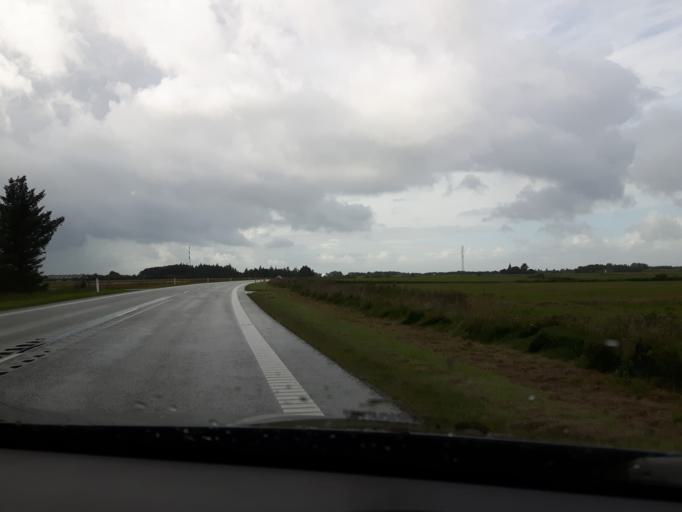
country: DK
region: North Denmark
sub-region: Jammerbugt Kommune
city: Fjerritslev
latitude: 57.0513
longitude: 9.1769
